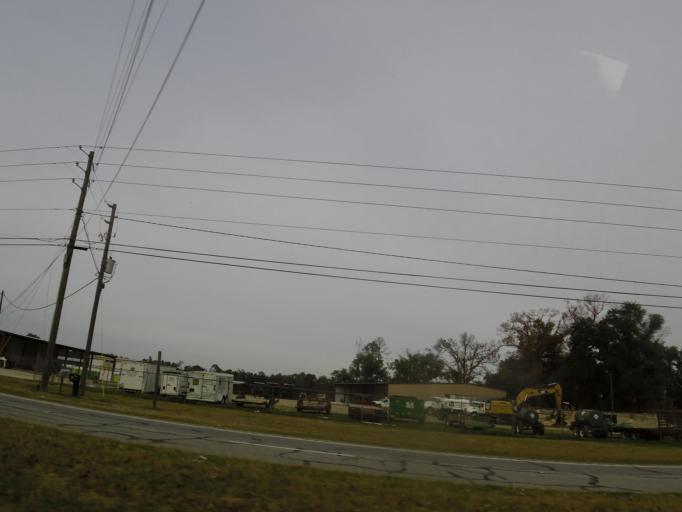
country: US
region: Georgia
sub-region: Decatur County
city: Bainbridge
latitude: 30.9264
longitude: -84.6184
